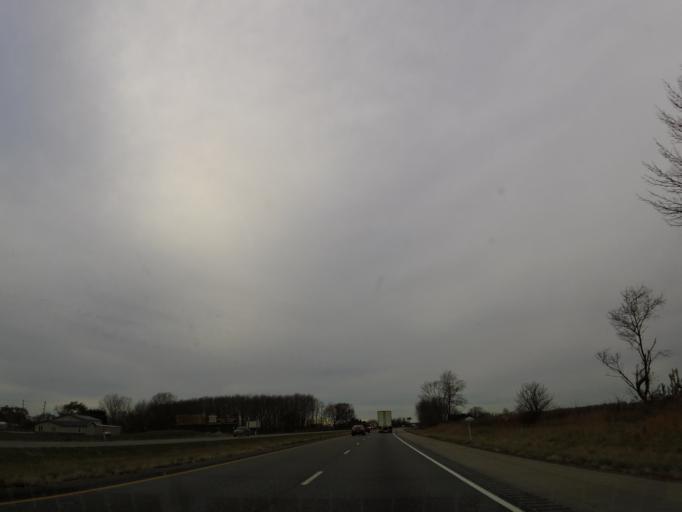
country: US
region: Indiana
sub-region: Hendricks County
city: Pittsboro
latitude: 39.8799
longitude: -86.5010
